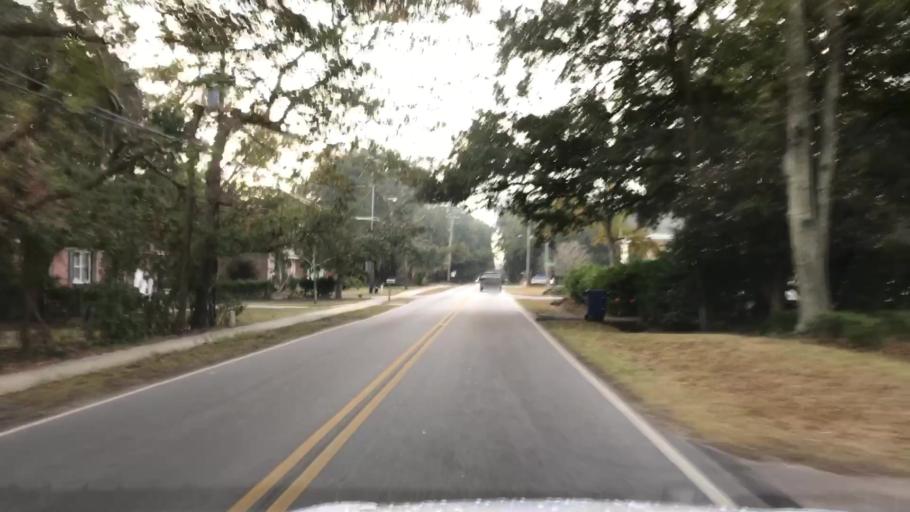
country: US
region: South Carolina
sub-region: Charleston County
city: North Charleston
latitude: 32.8044
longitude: -80.0081
